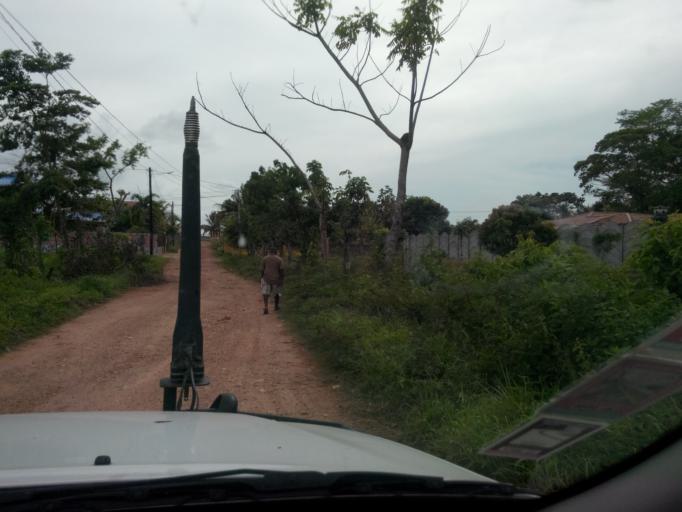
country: NI
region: Atlantico Sur
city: Bluefields
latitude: 12.0322
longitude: -83.7653
